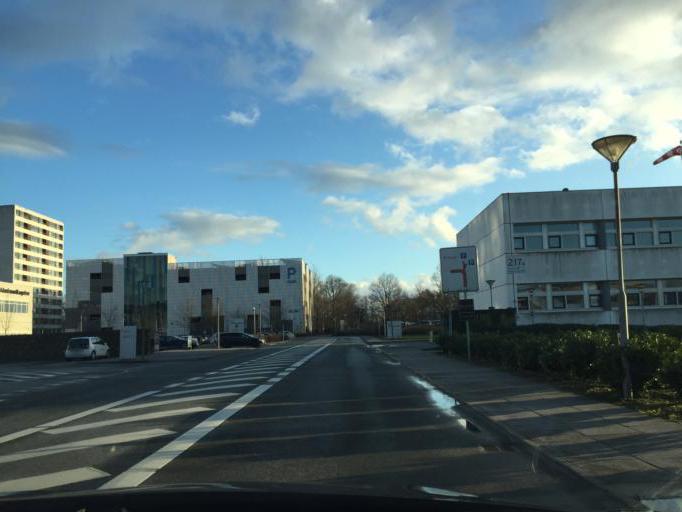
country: DK
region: South Denmark
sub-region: Odense Kommune
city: Odense
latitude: 55.3845
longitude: 10.3647
